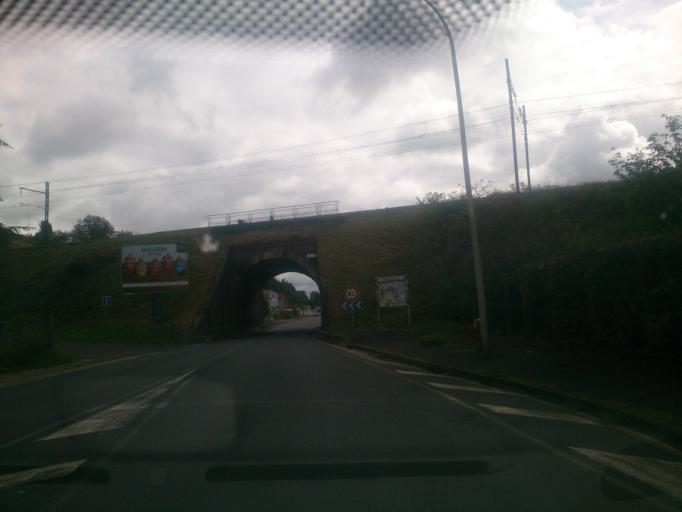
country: FR
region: Limousin
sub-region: Departement de la Correze
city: Saint-Pantaleon-de-Larche
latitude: 45.1617
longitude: 1.4837
